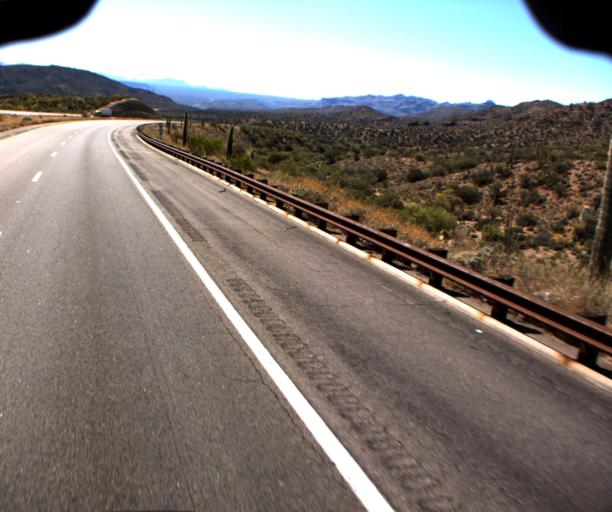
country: US
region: Arizona
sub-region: Yavapai County
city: Bagdad
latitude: 34.4362
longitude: -113.2578
